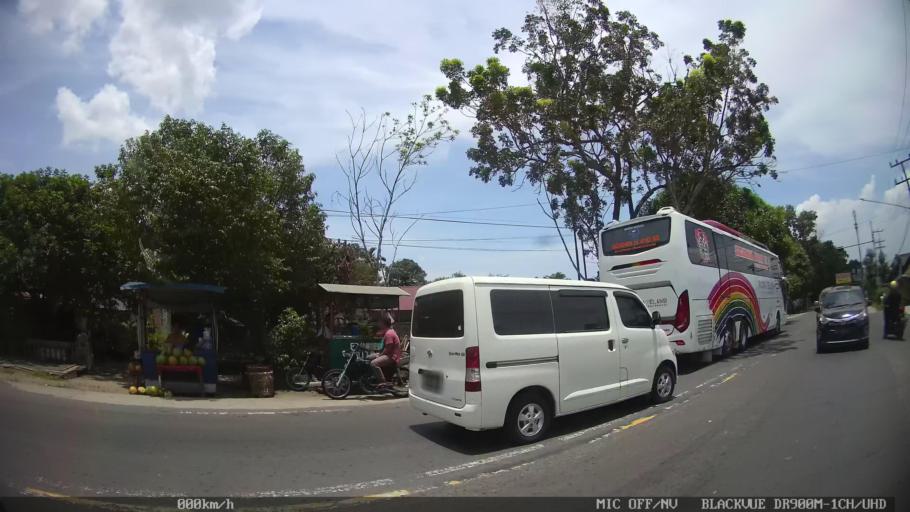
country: ID
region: North Sumatra
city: Binjai
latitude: 3.6279
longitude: 98.5087
